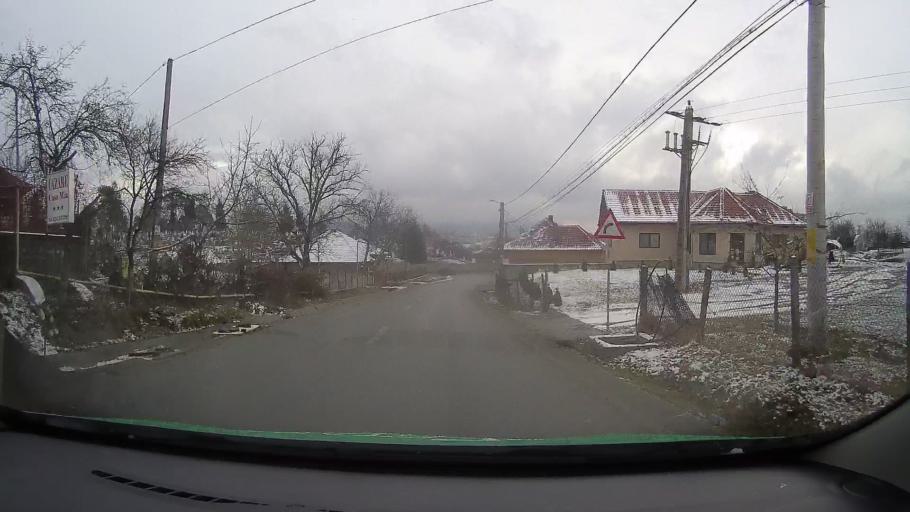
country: RO
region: Hunedoara
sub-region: Oras Hateg
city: Hateg
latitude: 45.6165
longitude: 22.9438
